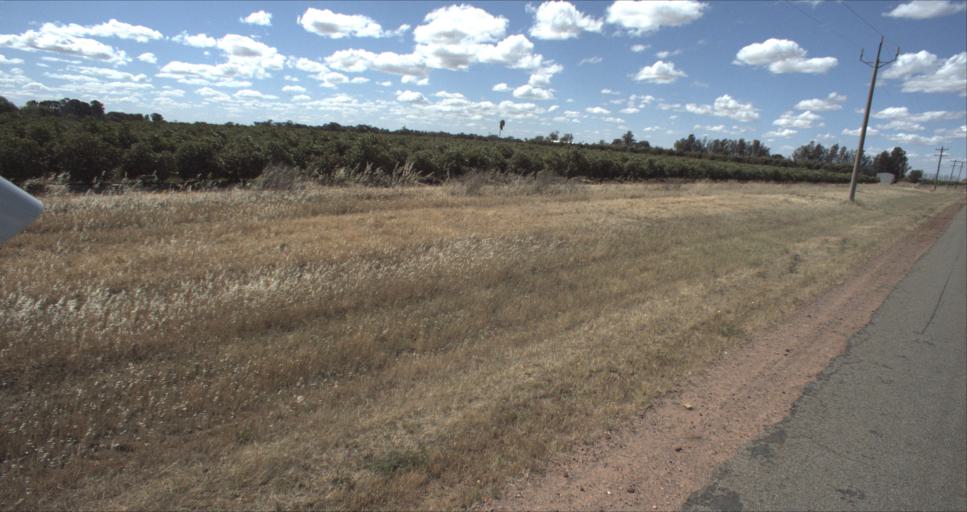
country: AU
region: New South Wales
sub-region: Leeton
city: Leeton
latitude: -34.5144
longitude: 146.2396
